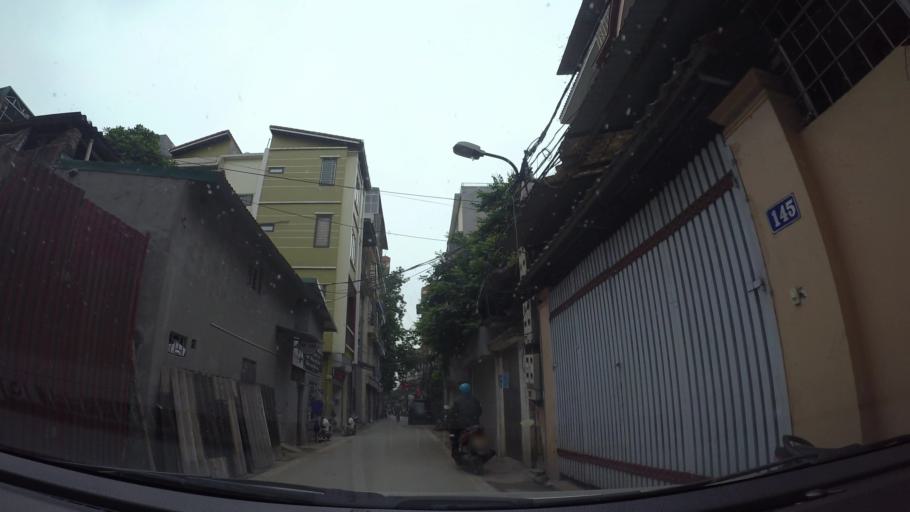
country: VN
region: Ha Noi
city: Tay Ho
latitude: 21.0679
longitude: 105.8350
